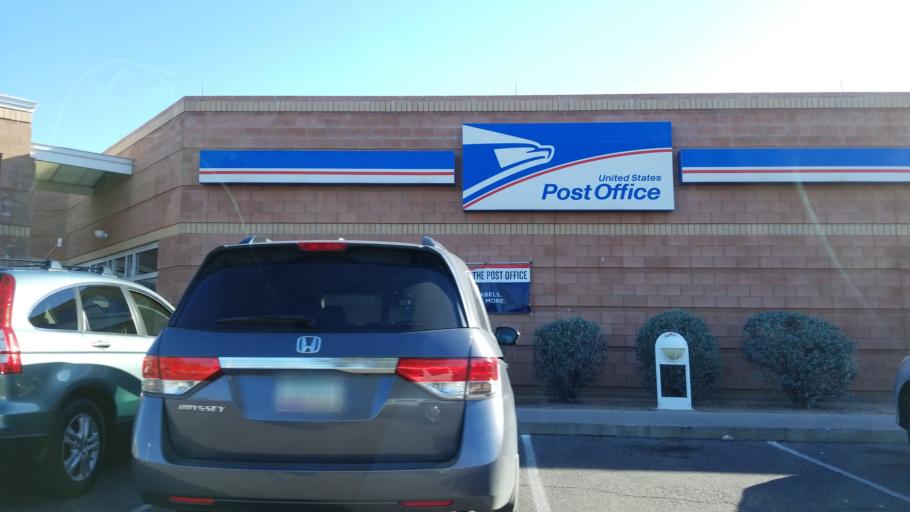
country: US
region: Arizona
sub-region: Maricopa County
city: Carefree
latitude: 33.6910
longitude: -111.9216
